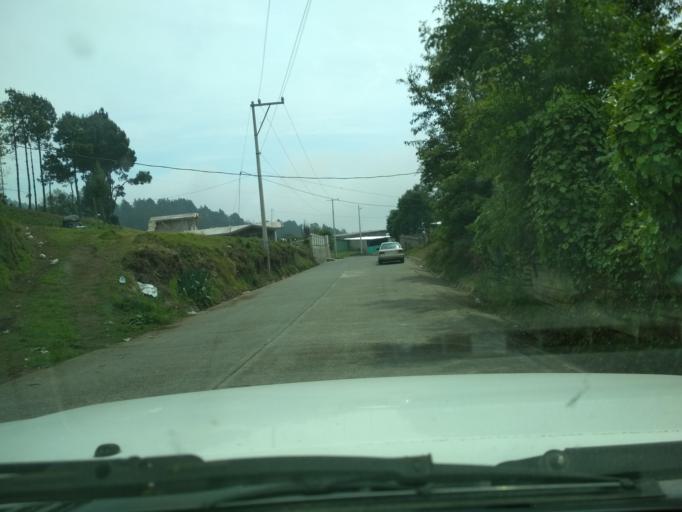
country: MX
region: Veracruz
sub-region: Mariano Escobedo
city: San Isidro el Berro
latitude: 18.9761
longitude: -97.2066
